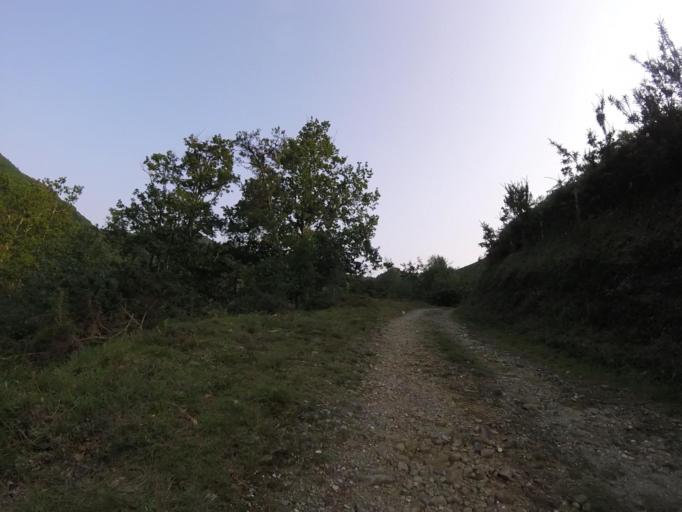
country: ES
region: Navarre
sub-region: Provincia de Navarra
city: Arano
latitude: 43.2553
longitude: -1.8442
